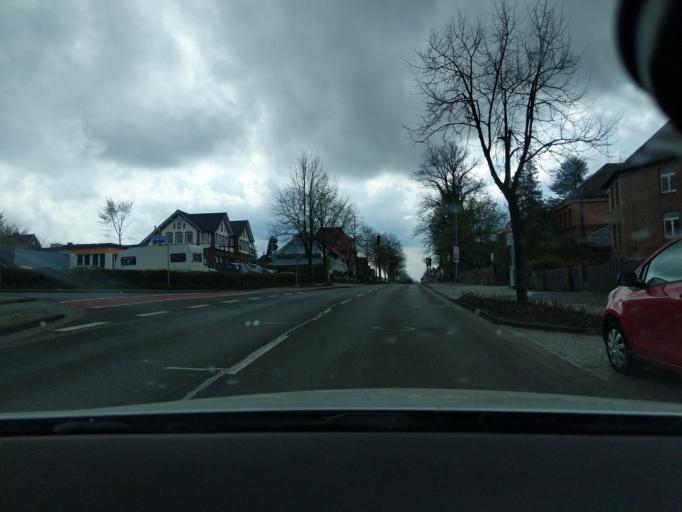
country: DE
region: Lower Saxony
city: Stade
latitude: 53.5914
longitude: 9.4728
